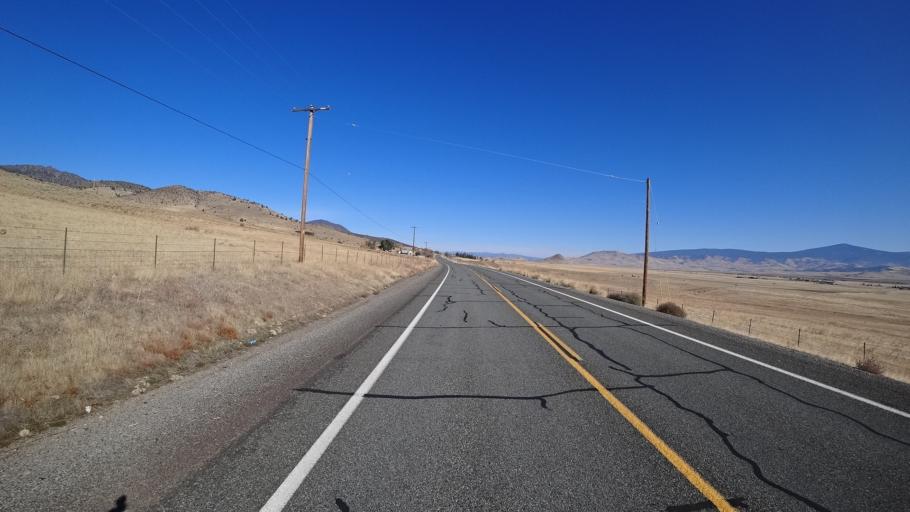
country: US
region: California
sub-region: Siskiyou County
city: Montague
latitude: 41.7809
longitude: -122.5206
